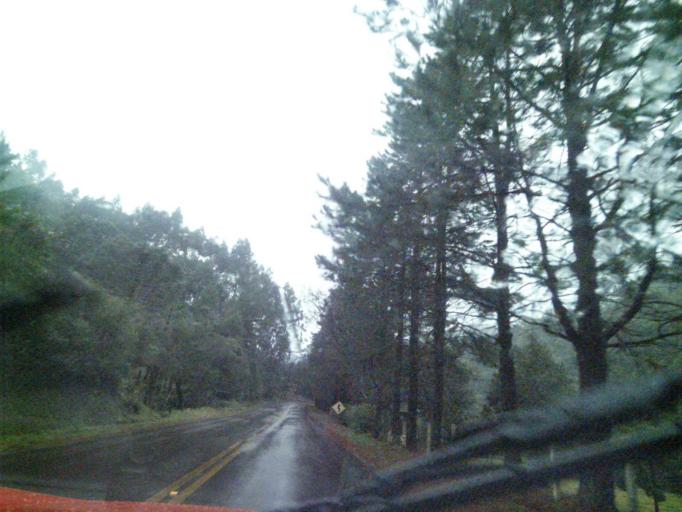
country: BR
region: Santa Catarina
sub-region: Anitapolis
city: Anitapolis
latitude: -27.7962
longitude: -49.0446
